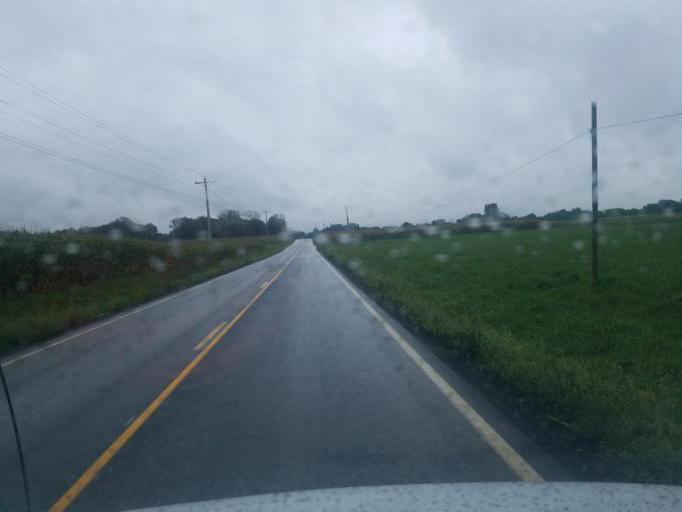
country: US
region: Ohio
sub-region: Wayne County
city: West Salem
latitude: 40.9154
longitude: -82.1220
